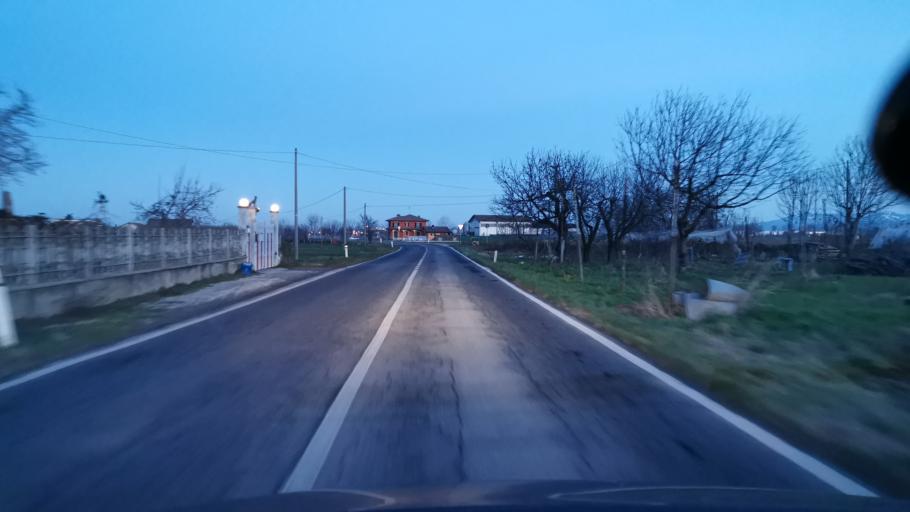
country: IT
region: Piedmont
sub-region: Provincia di Cuneo
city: Roata Rossi
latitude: 44.4400
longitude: 7.5474
